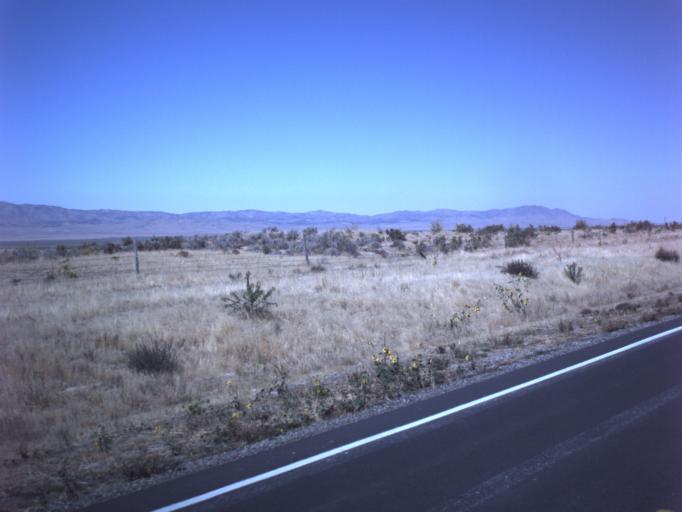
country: US
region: Utah
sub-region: Tooele County
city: Grantsville
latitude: 40.5071
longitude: -112.7479
